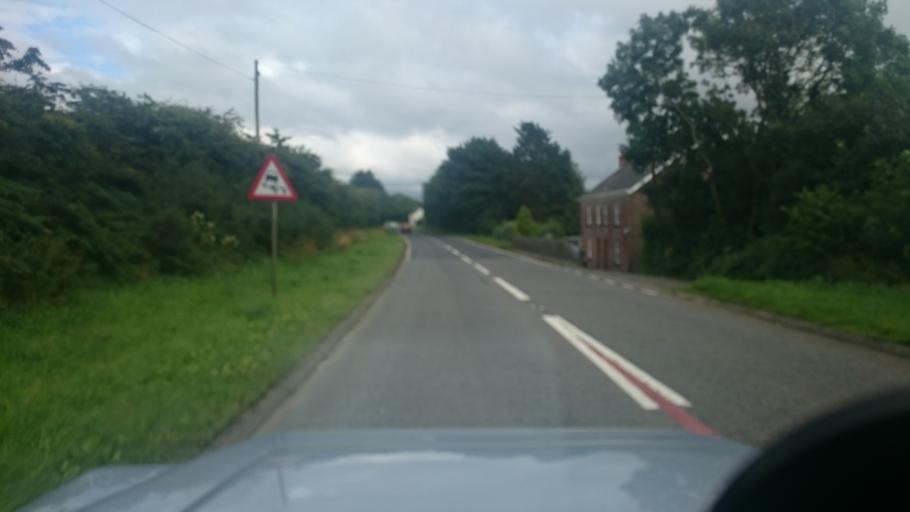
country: GB
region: Wales
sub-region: Pembrokeshire
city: Wiston
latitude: 51.8037
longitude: -4.8615
